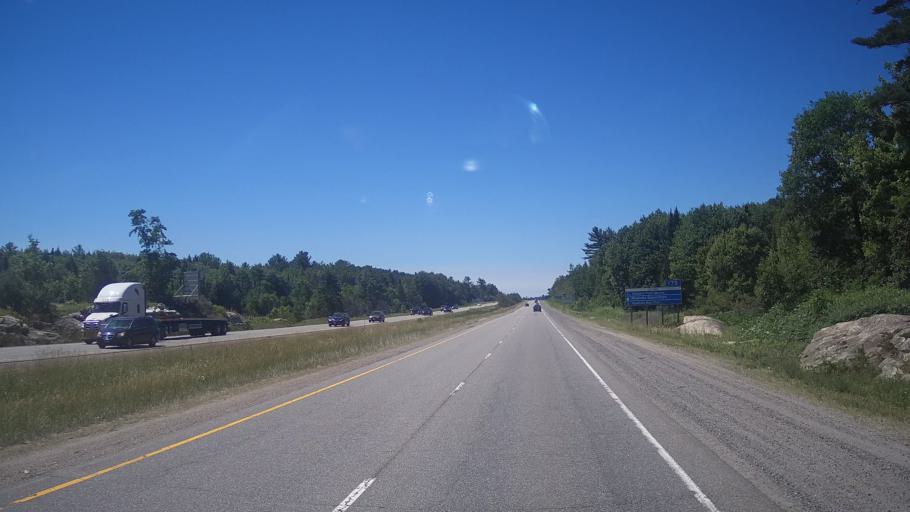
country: CA
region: Ontario
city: Gravenhurst
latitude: 44.9559
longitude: -79.3296
